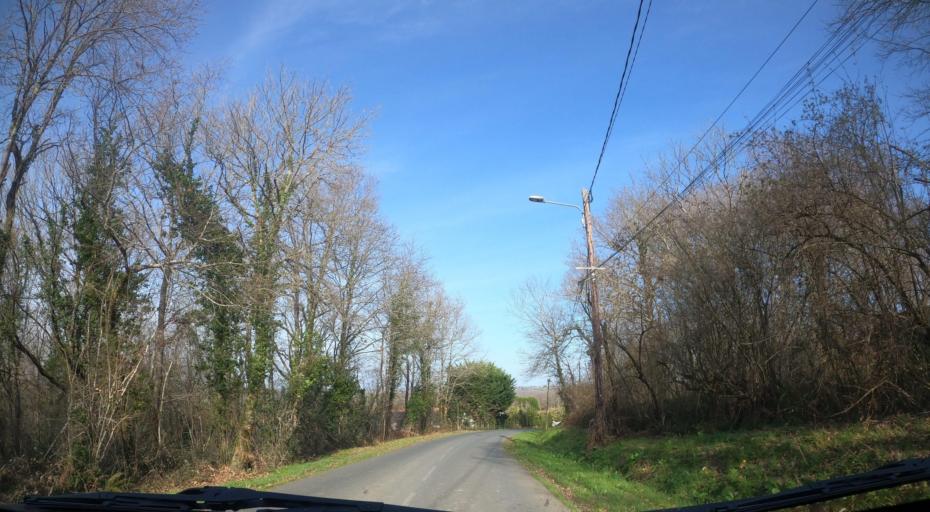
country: FR
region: Aquitaine
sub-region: Departement des Pyrenees-Atlantiques
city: Briscous
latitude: 43.4393
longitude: -1.3749
